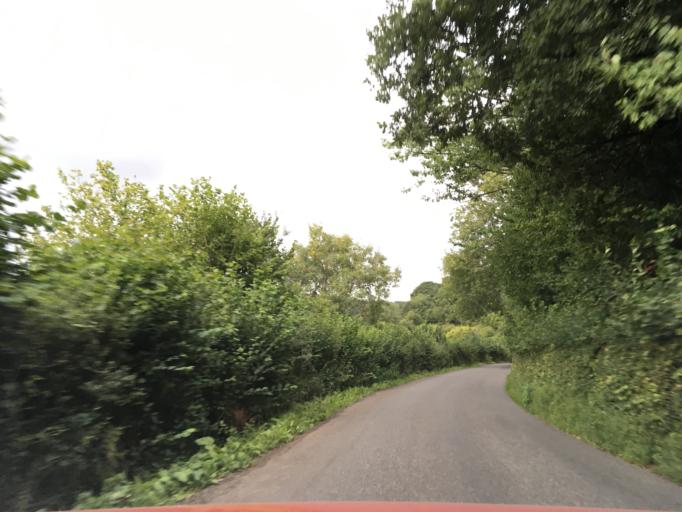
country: GB
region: Wales
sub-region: Newport
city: Llanvaches
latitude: 51.6340
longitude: -2.8212
